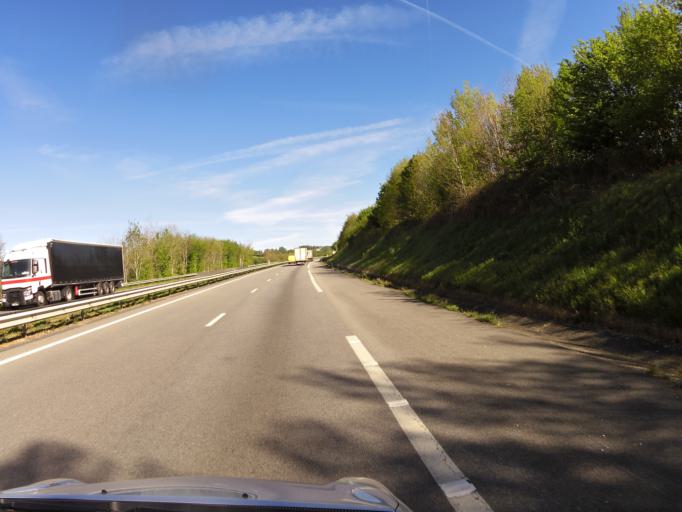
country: FR
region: Limousin
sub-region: Departement de la Correze
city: Vigeois
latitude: 45.4266
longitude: 1.5143
